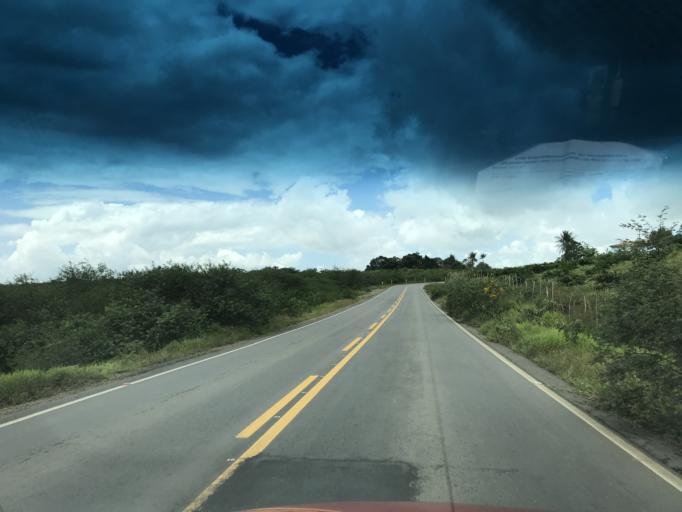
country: BR
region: Bahia
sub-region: Conceicao Do Almeida
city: Conceicao do Almeida
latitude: -12.7004
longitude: -39.2379
